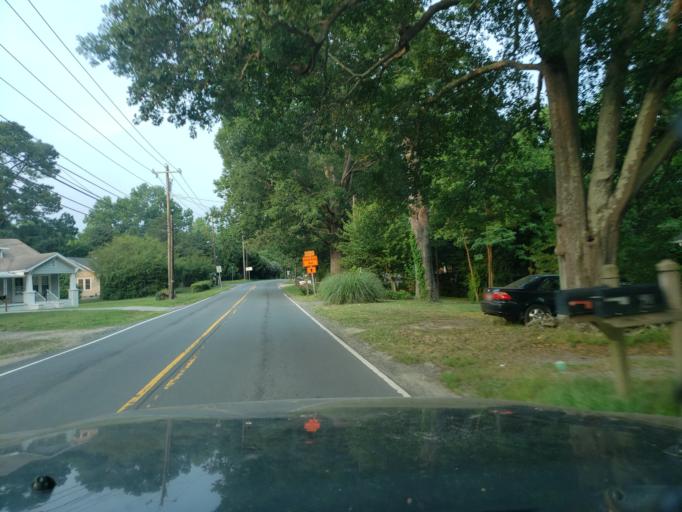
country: US
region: North Carolina
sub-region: Durham County
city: Durham
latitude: 35.9650
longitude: -78.8525
